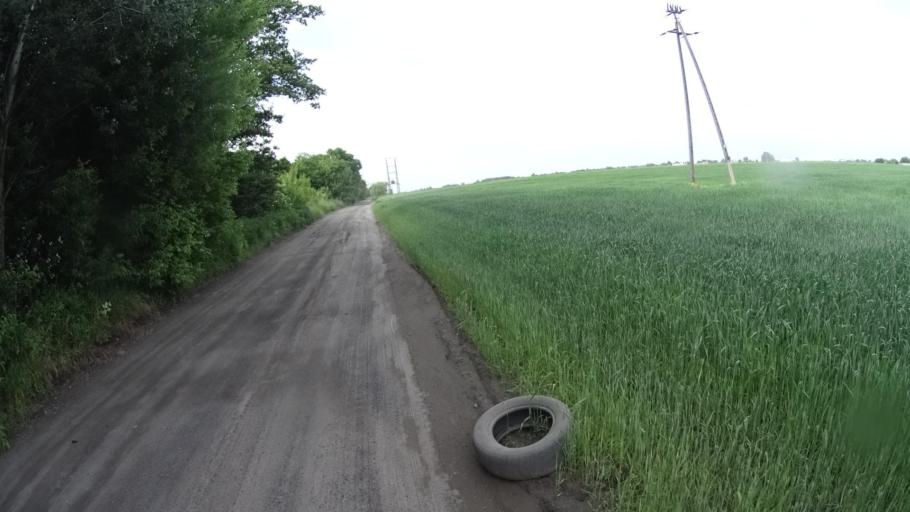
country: PL
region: Masovian Voivodeship
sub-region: Powiat warszawski zachodni
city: Jozefow
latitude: 52.1981
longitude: 20.7428
